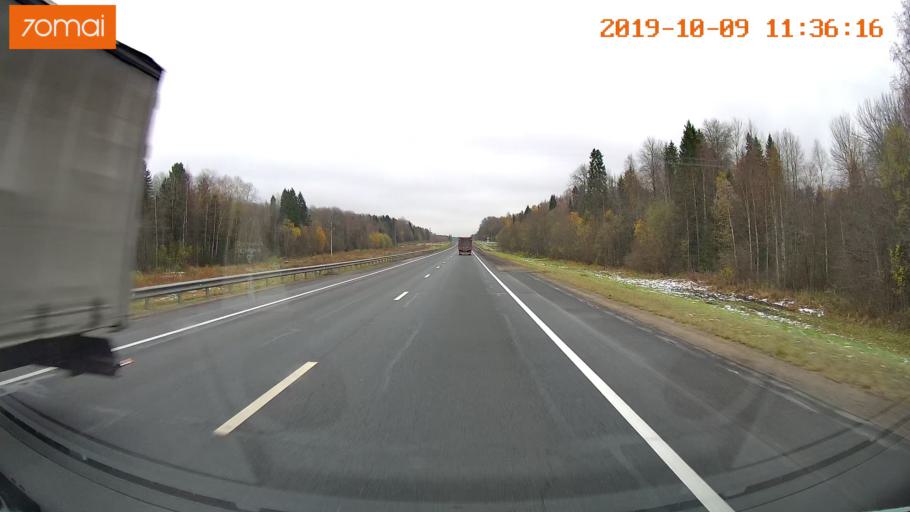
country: RU
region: Vologda
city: Gryazovets
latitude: 58.9928
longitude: 40.1349
